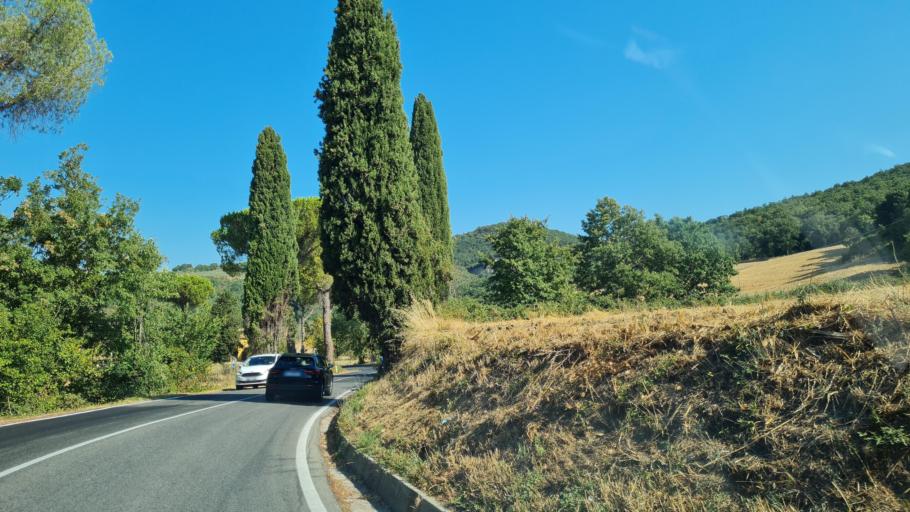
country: IT
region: Tuscany
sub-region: Provincia di Siena
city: Chianciano Terme
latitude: 43.0294
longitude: 11.7713
